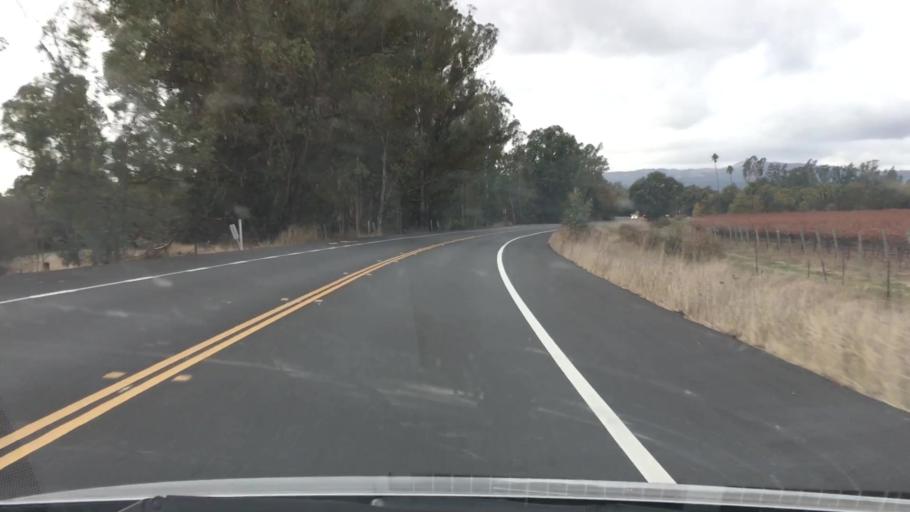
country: US
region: California
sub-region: Sonoma County
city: Sonoma
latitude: 38.2700
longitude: -122.4193
